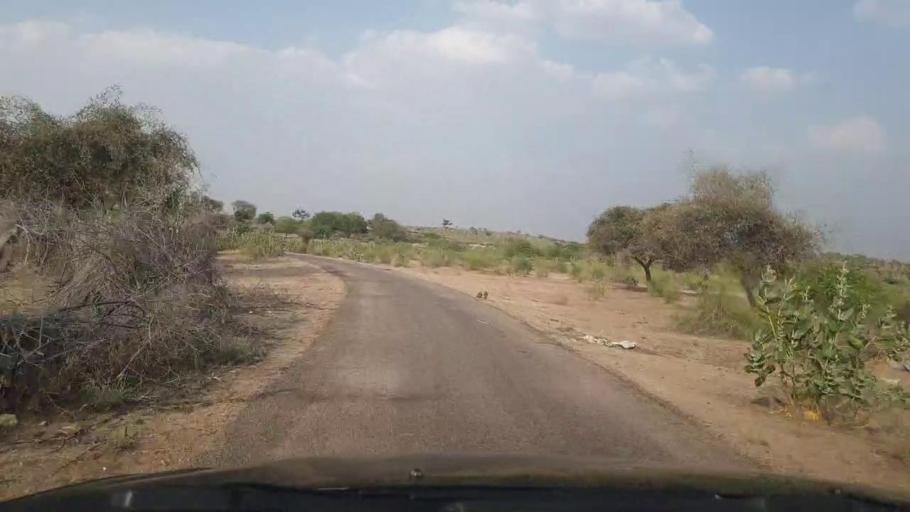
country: PK
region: Sindh
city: Islamkot
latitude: 25.0659
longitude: 70.5655
